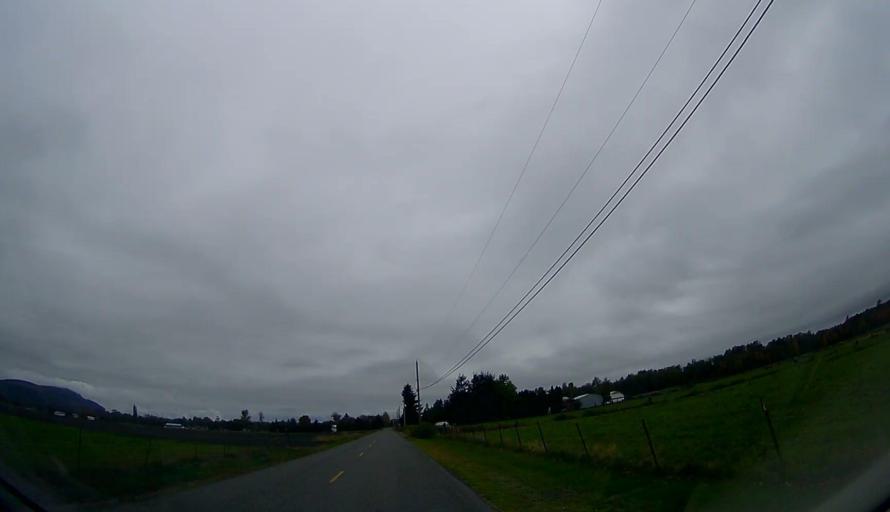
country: US
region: Washington
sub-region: Skagit County
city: Sedro-Woolley
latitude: 48.5146
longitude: -122.1532
